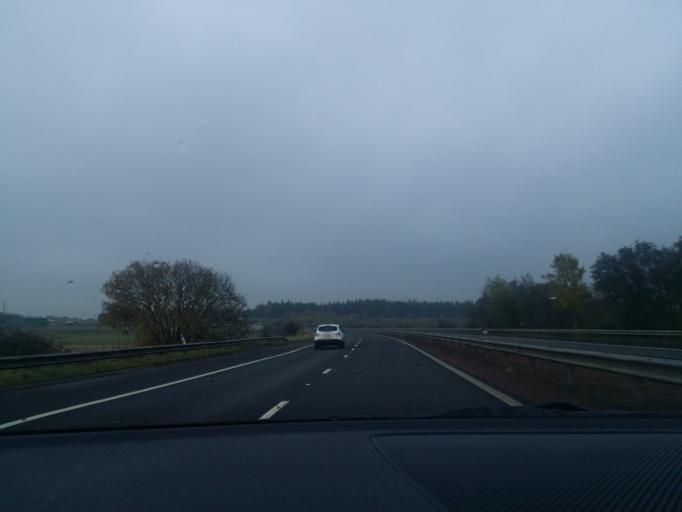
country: GB
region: Scotland
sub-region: Falkirk
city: Larbert
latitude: 56.0465
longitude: -3.8272
